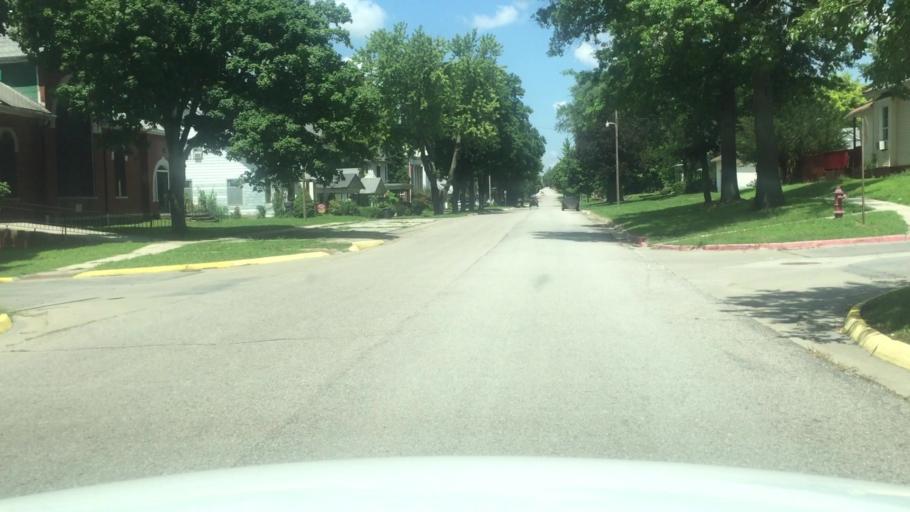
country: US
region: Kansas
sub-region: Brown County
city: Horton
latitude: 39.6630
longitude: -95.5273
